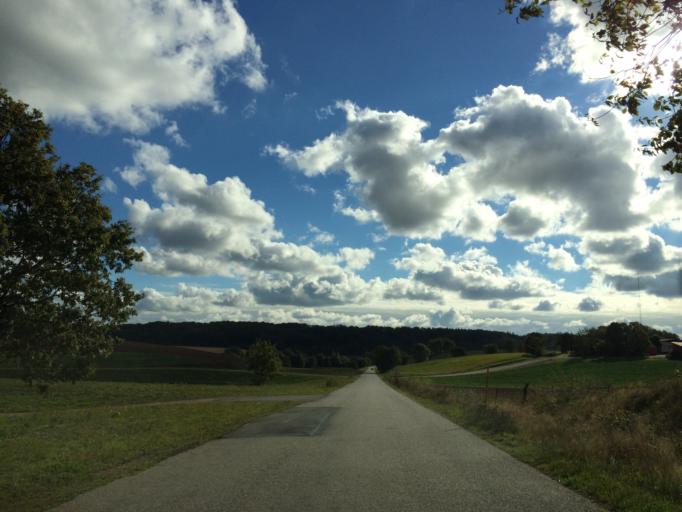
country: DK
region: Central Jutland
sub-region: Skanderborg Kommune
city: Ry
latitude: 56.1701
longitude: 9.7731
